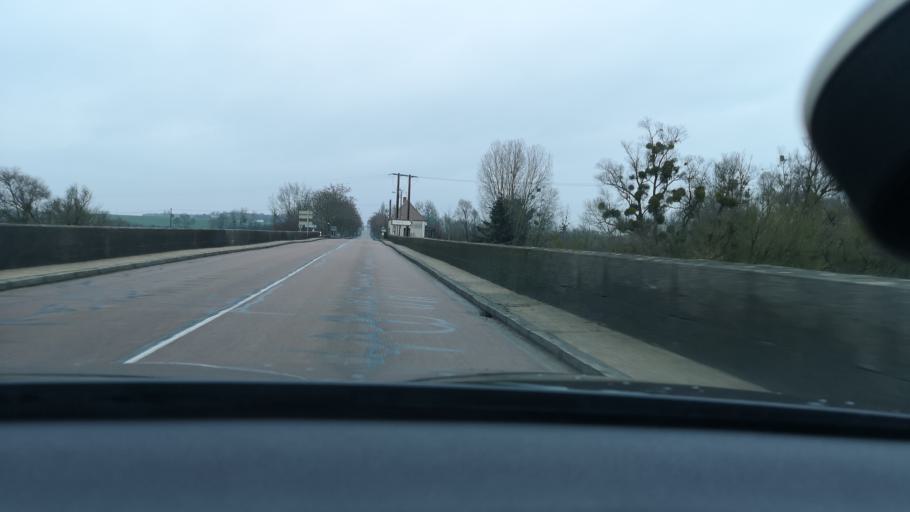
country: FR
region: Bourgogne
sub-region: Departement de la Cote-d'Or
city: Seurre
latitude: 46.9389
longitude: 5.1497
